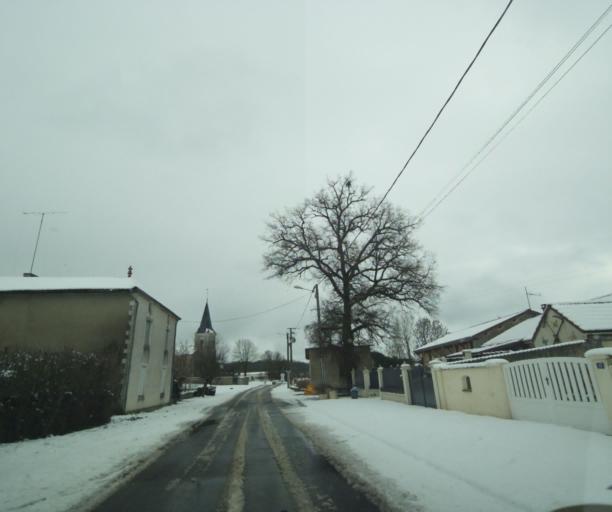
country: FR
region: Champagne-Ardenne
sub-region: Departement de la Haute-Marne
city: Montier-en-Der
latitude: 48.4131
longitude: 4.7368
